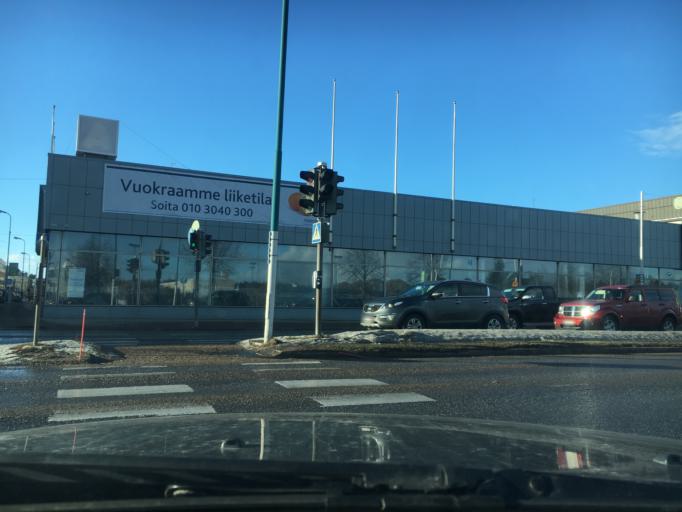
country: FI
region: Kainuu
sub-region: Kajaani
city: Kajaani
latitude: 64.2246
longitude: 27.7342
